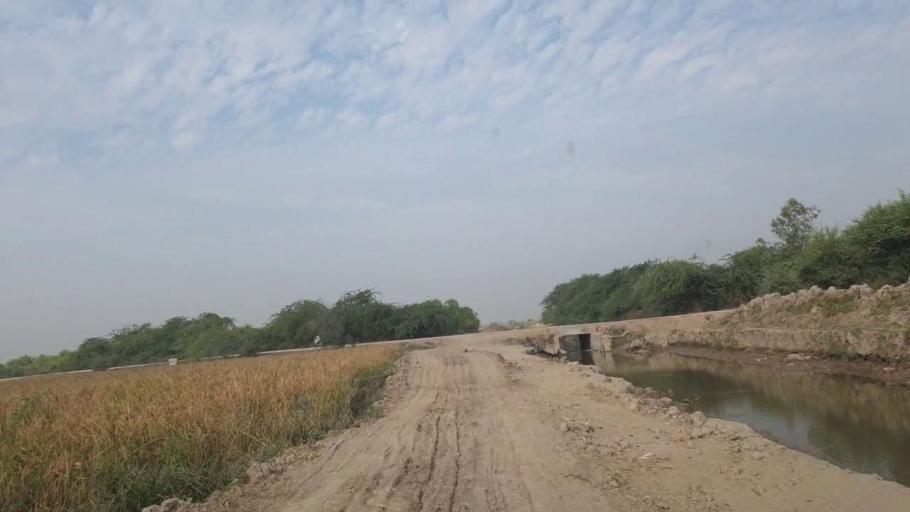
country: PK
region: Sindh
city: Tando Bago
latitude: 24.8820
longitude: 68.9367
